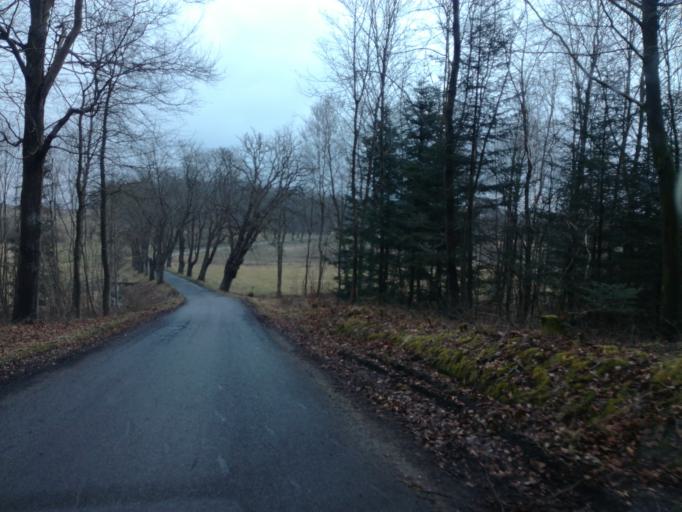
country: DK
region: South Denmark
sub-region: Vejle Kommune
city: Brejning
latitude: 55.6195
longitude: 9.7092
